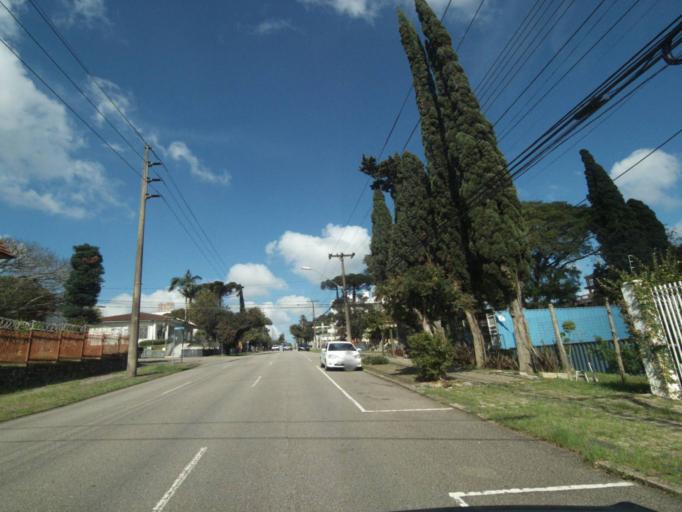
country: BR
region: Parana
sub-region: Curitiba
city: Curitiba
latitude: -25.4180
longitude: -49.2808
